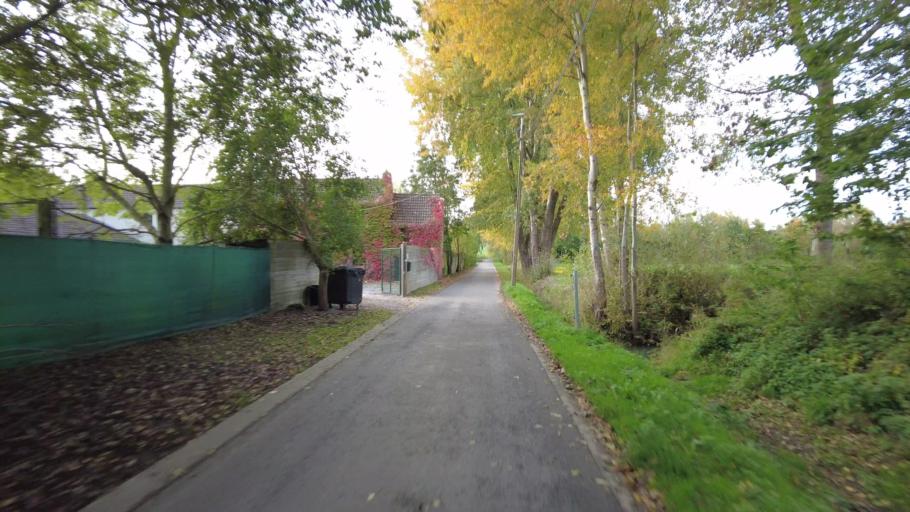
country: BE
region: Flanders
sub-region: Provincie Vlaams-Brabant
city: Hoegaarden
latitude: 50.7635
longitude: 4.8920
